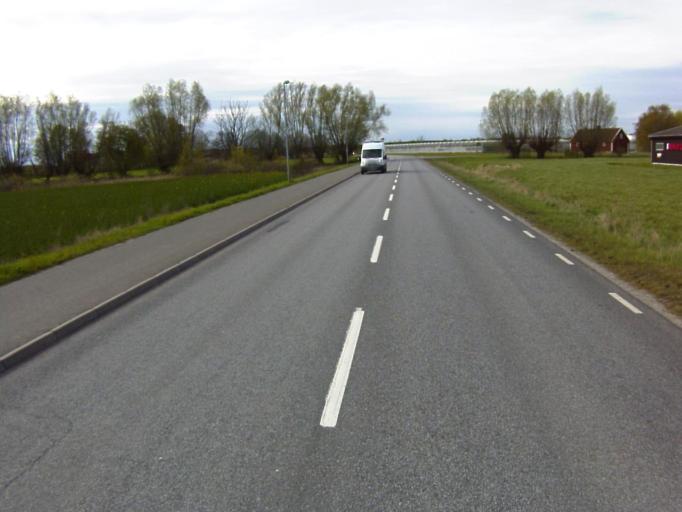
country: SE
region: Skane
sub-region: Kristianstads Kommun
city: Kristianstad
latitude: 56.0128
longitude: 14.1251
